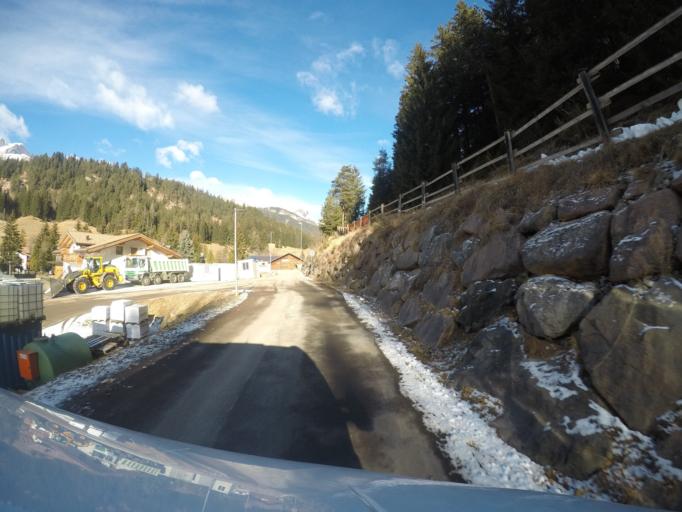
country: IT
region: Trentino-Alto Adige
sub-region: Provincia di Trento
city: Soraga
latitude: 46.3997
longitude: 11.6731
